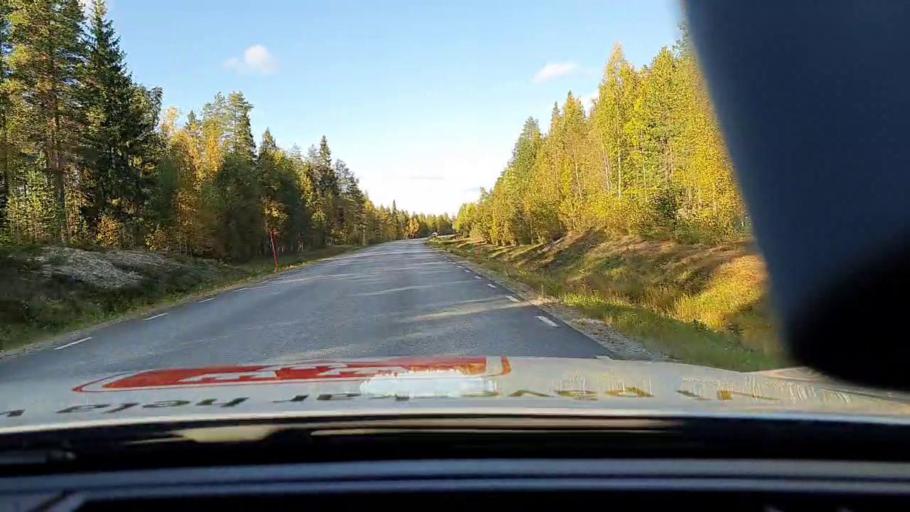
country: SE
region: Norrbotten
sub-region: Pitea Kommun
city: Norrfjarden
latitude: 65.4984
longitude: 21.4755
